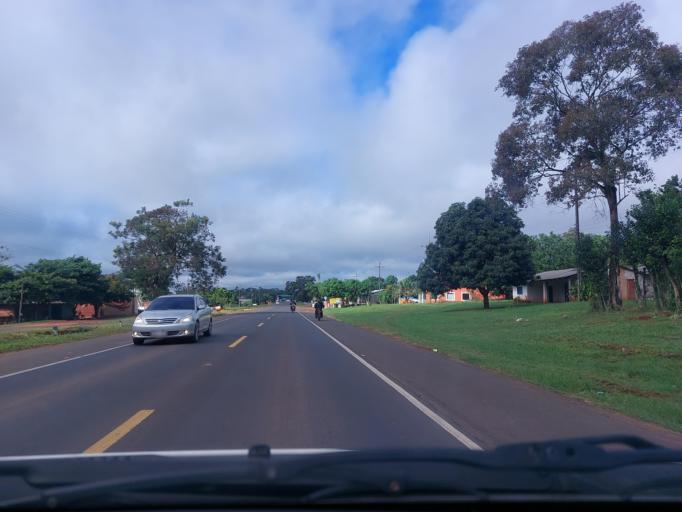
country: PY
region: San Pedro
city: Guayaybi
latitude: -24.5771
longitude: -56.4024
